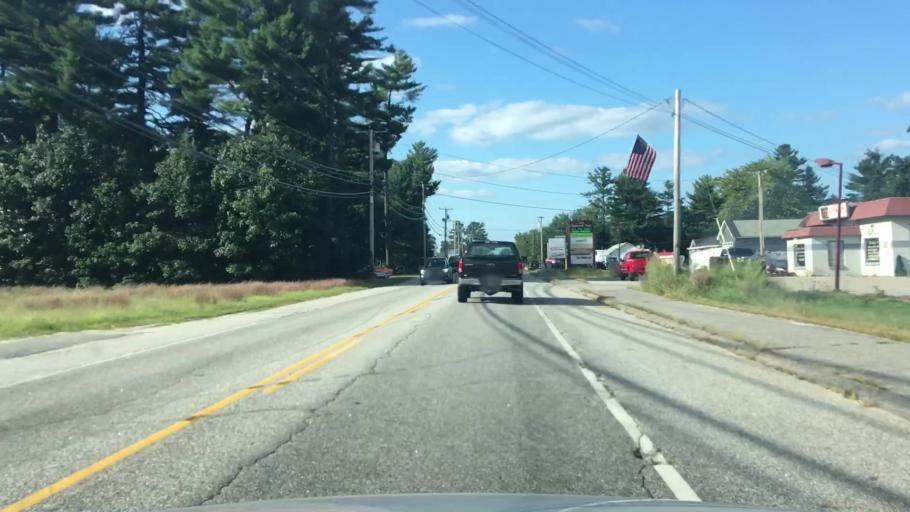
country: US
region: Maine
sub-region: Cumberland County
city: North Windham
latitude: 43.8214
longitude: -70.4341
